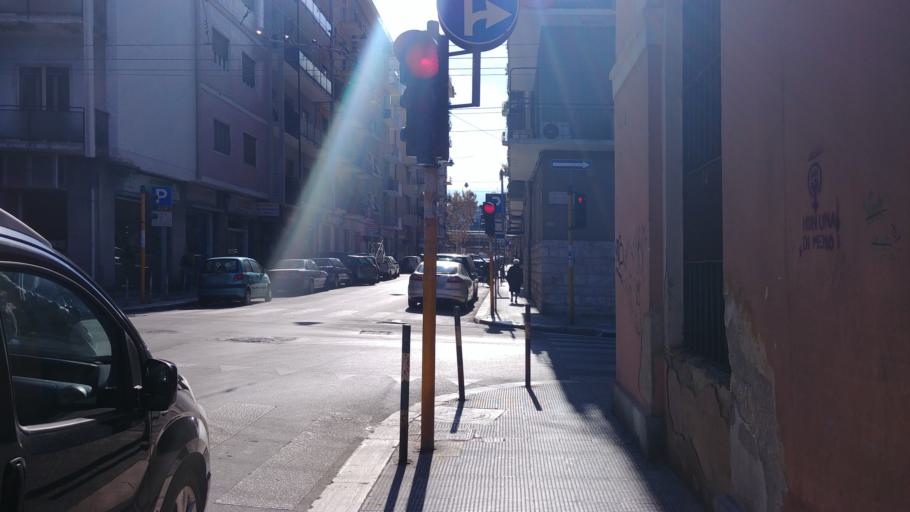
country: IT
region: Apulia
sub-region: Provincia di Bari
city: Bari
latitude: 41.1194
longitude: 16.8589
